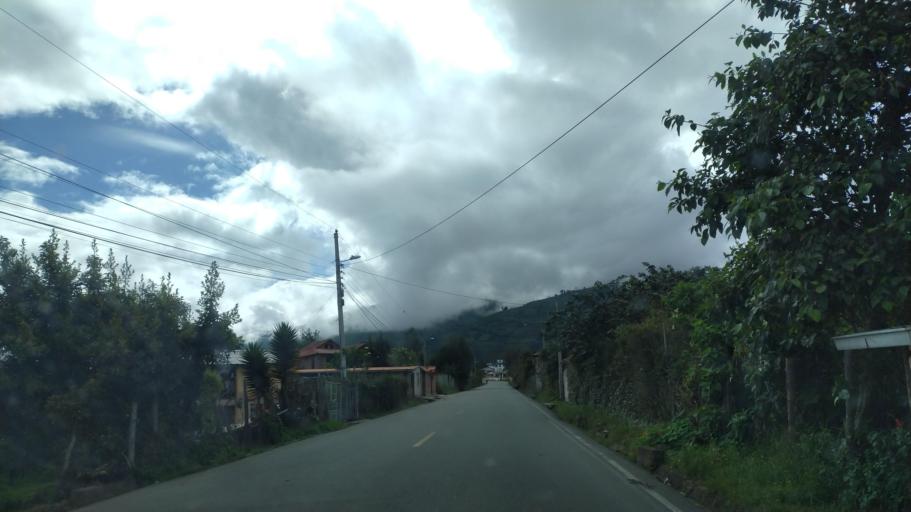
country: EC
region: Chimborazo
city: Riobamba
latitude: -1.6592
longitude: -78.5756
